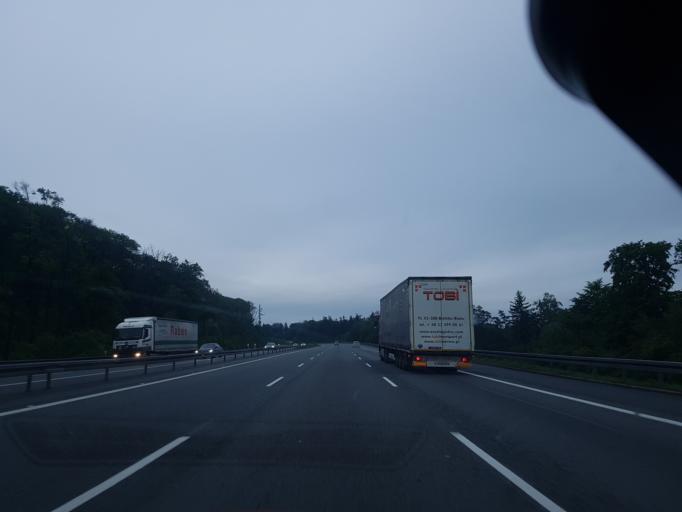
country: PL
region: Opole Voivodeship
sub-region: Powiat krapkowicki
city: Zdzieszowice
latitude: 50.4757
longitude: 18.1373
